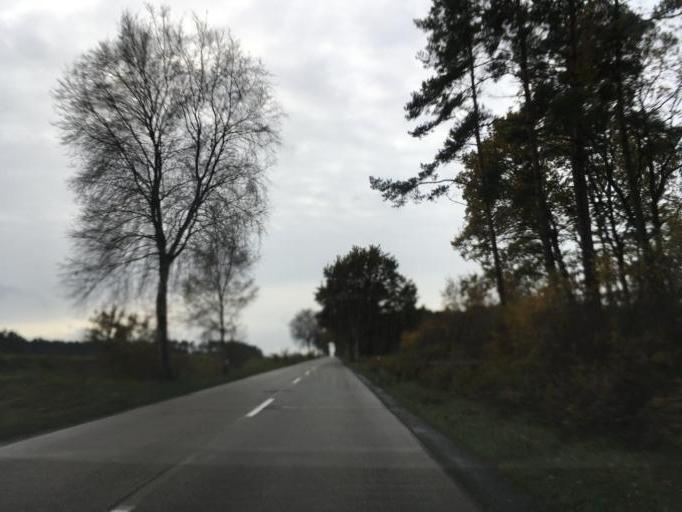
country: DE
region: Lower Saxony
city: Sudergellersen
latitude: 53.1826
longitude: 10.2735
